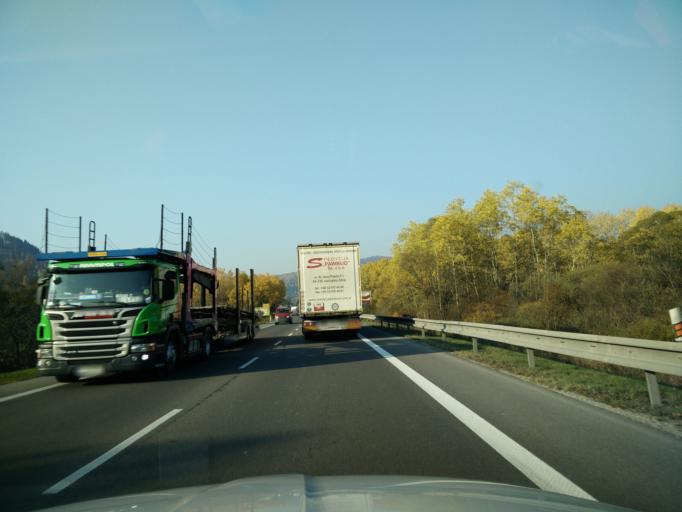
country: SK
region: Zilinsky
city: Cadca
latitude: 49.4097
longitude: 18.8422
